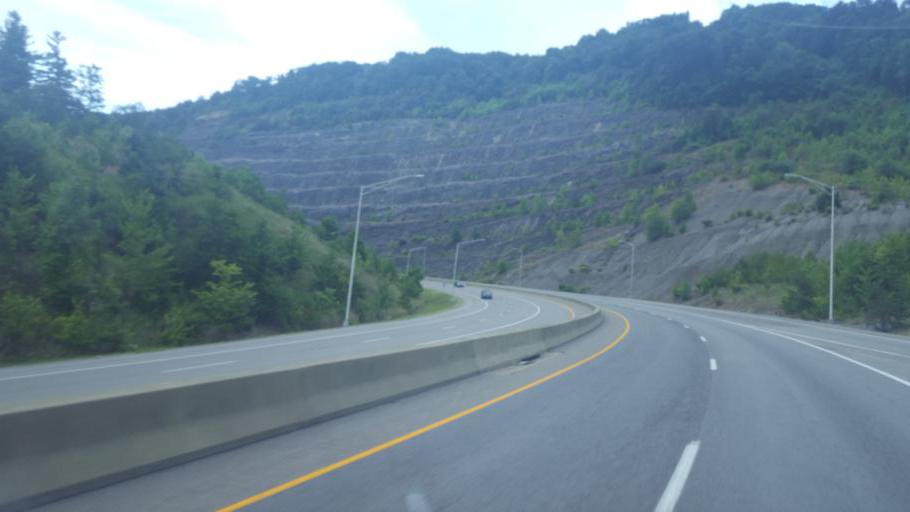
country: US
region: Kentucky
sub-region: Letcher County
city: Jenkins
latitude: 37.1581
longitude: -82.6487
